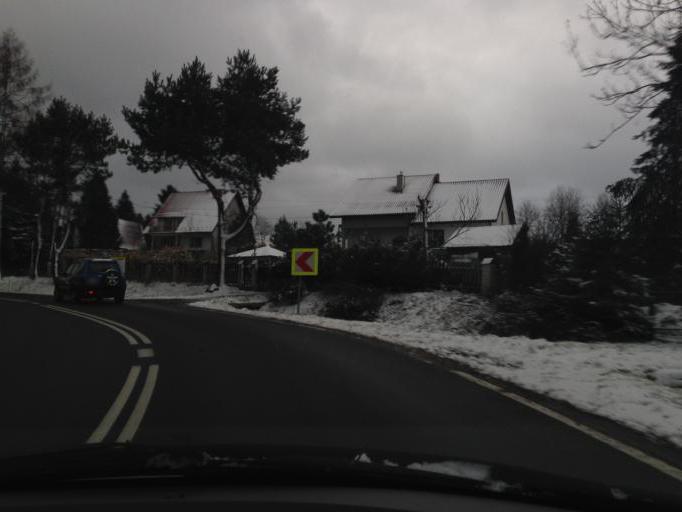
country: PL
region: Lesser Poland Voivodeship
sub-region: Powiat tarnowski
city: Siemiechow
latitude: 49.8457
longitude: 20.9320
